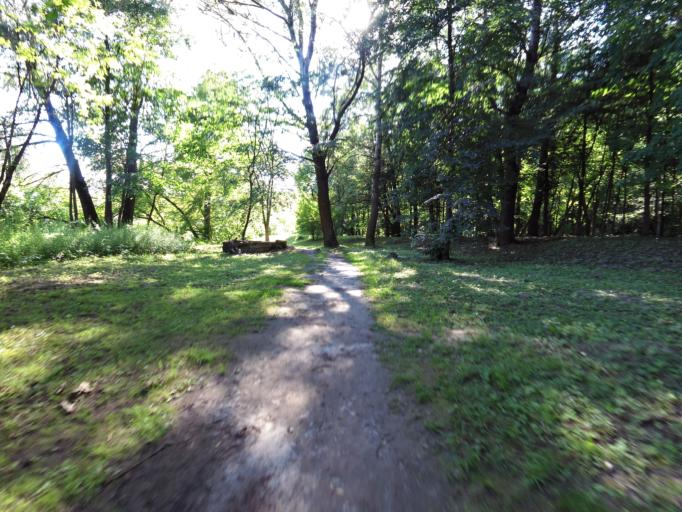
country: LT
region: Vilnius County
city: Vilkpede
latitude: 54.6896
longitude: 25.2309
